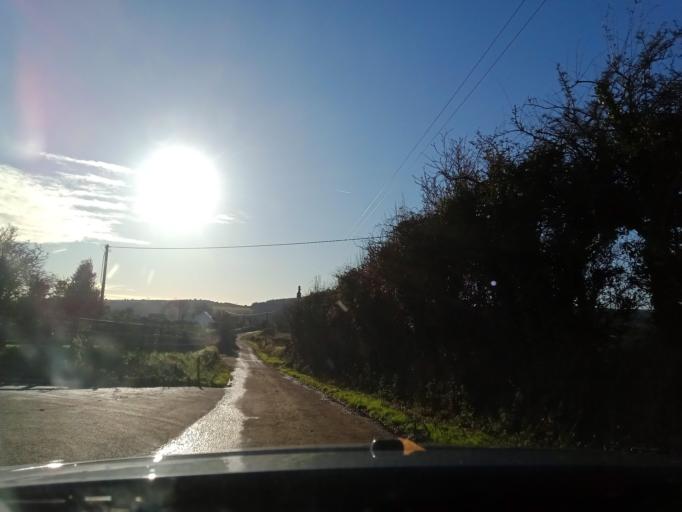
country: IE
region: Leinster
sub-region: Kilkenny
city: Mooncoin
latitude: 52.2676
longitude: -7.2384
